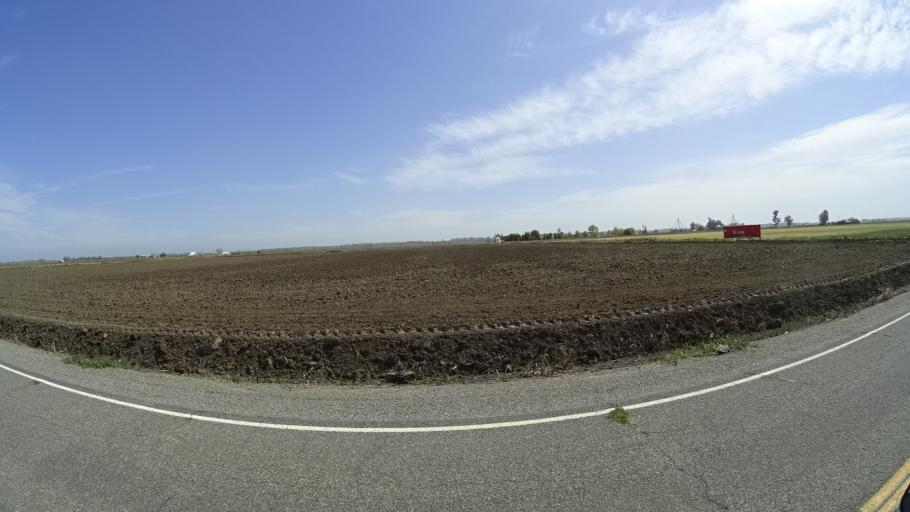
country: US
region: California
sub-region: Glenn County
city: Hamilton City
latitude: 39.5880
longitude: -122.0372
